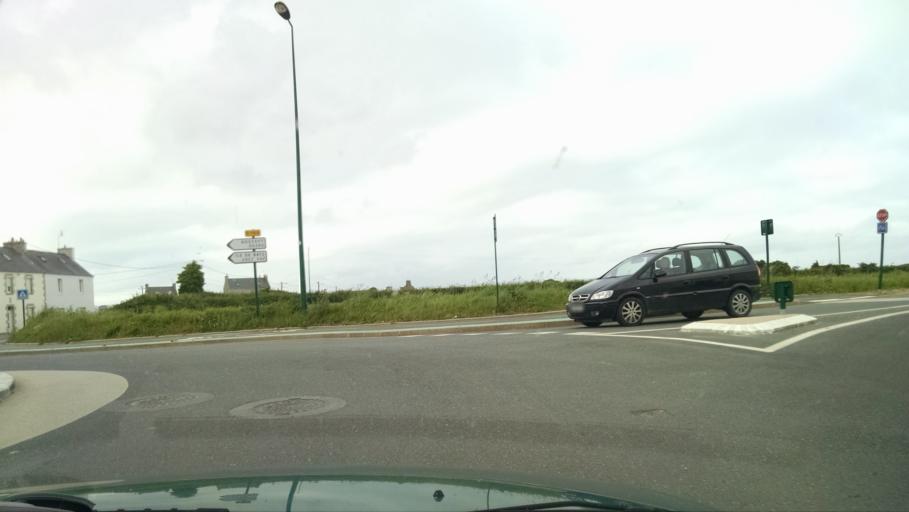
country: FR
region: Brittany
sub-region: Departement du Finistere
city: Saint-Pol-de-Leon
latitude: 48.6901
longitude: -3.9888
